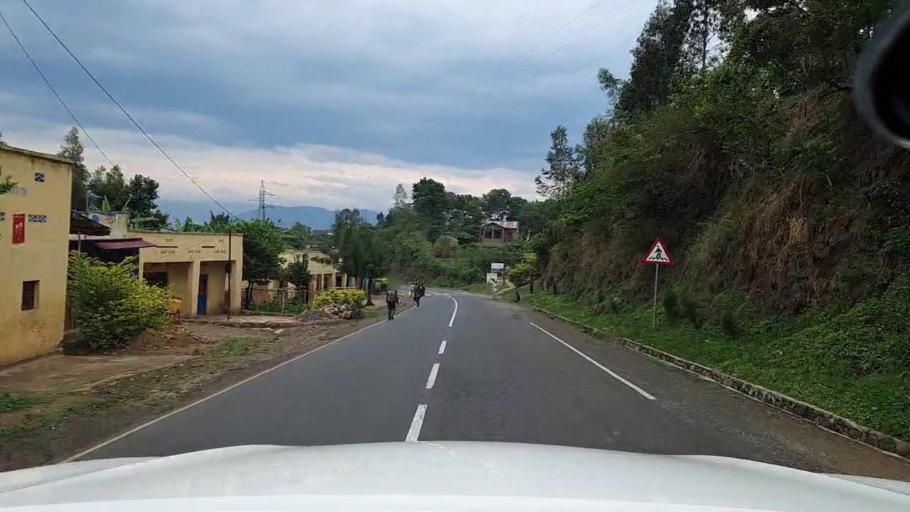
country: RW
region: Western Province
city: Cyangugu
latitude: -2.6585
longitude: 28.9763
